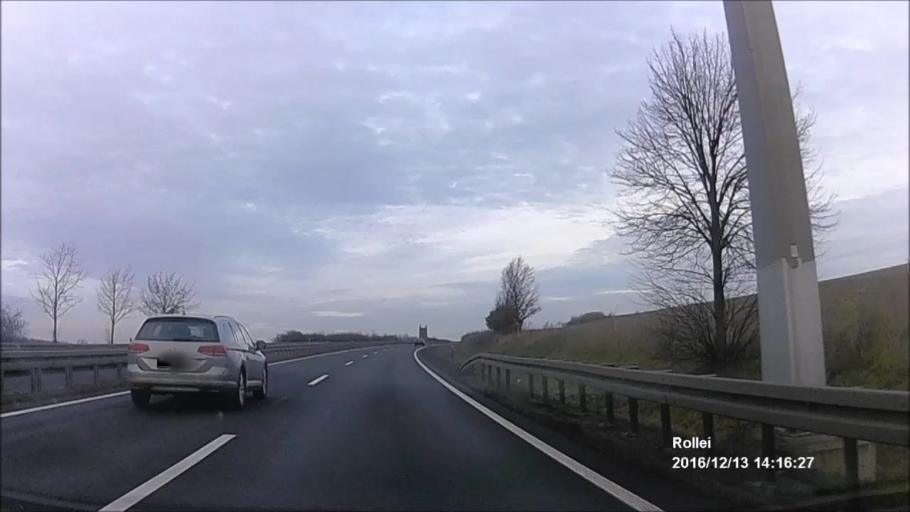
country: DE
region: Thuringia
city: Erfurt
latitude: 51.0171
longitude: 11.0581
